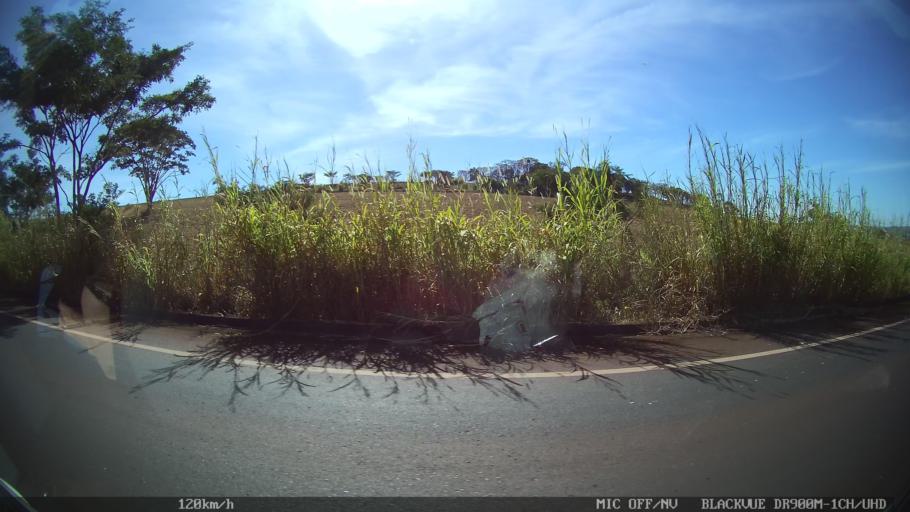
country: BR
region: Sao Paulo
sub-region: Sao Joaquim Da Barra
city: Sao Joaquim da Barra
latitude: -20.5613
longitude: -47.6874
